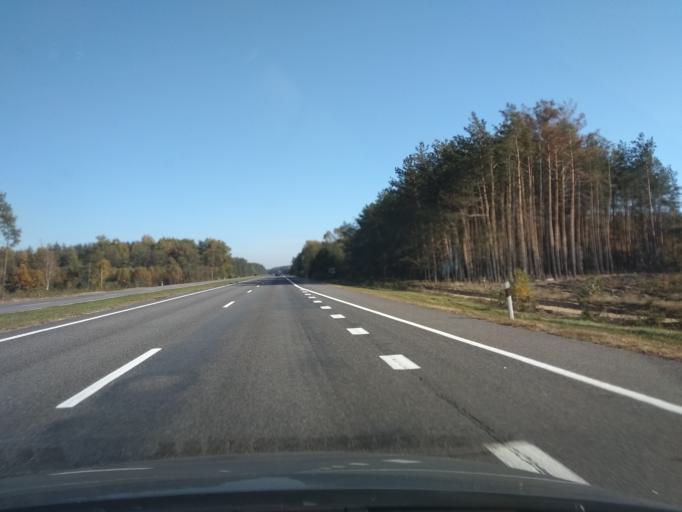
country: BY
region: Brest
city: Antopal'
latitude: 52.3577
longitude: 24.7028
